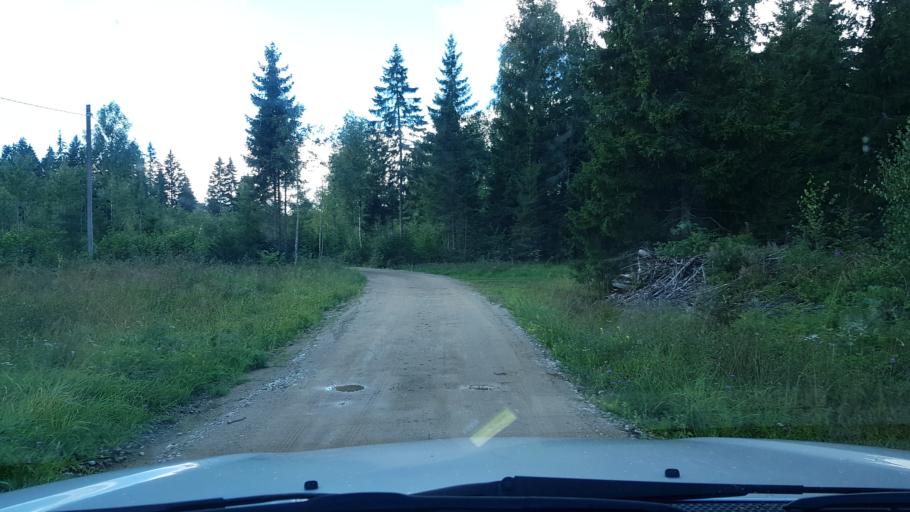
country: EE
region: Harju
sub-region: Raasiku vald
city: Arukula
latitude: 59.2538
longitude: 25.0977
